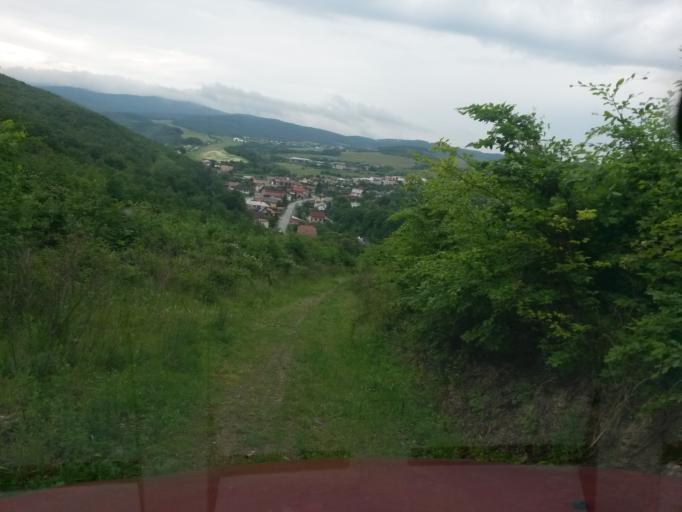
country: SK
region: Kosicky
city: Kosice
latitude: 48.7228
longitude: 21.1472
